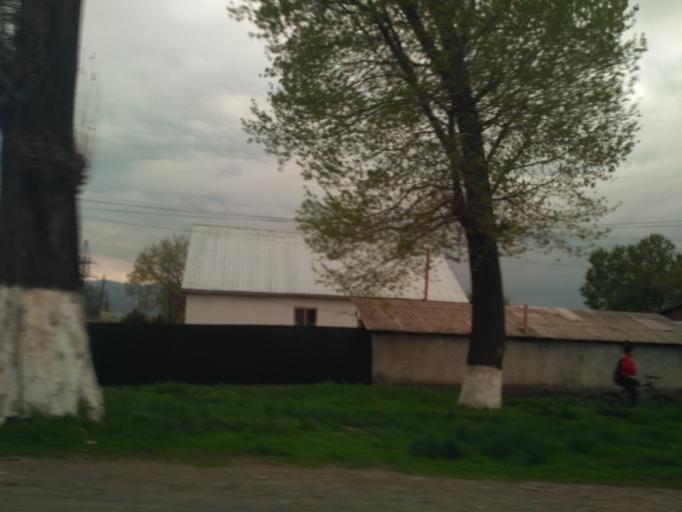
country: KZ
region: Almaty Oblysy
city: Burunday
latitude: 43.2106
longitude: 76.3287
